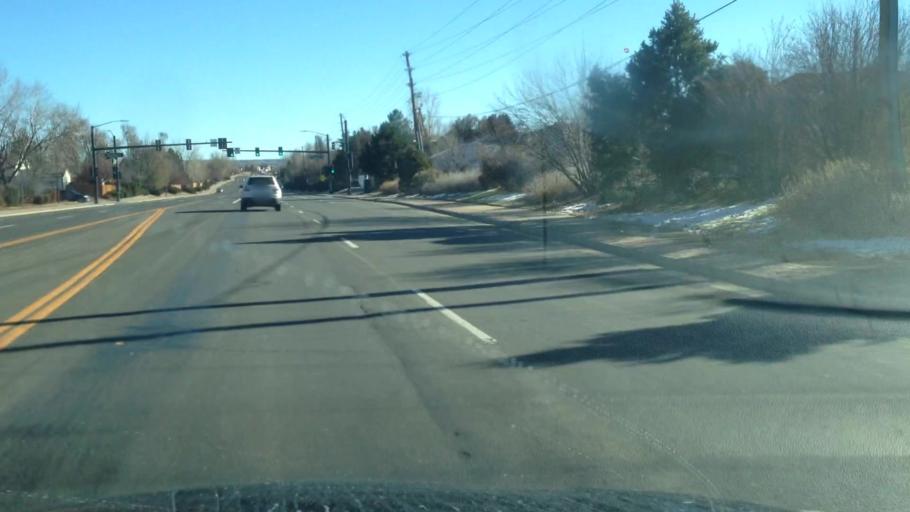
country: US
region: Colorado
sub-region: Arapahoe County
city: Dove Valley
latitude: 39.5659
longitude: -104.8013
